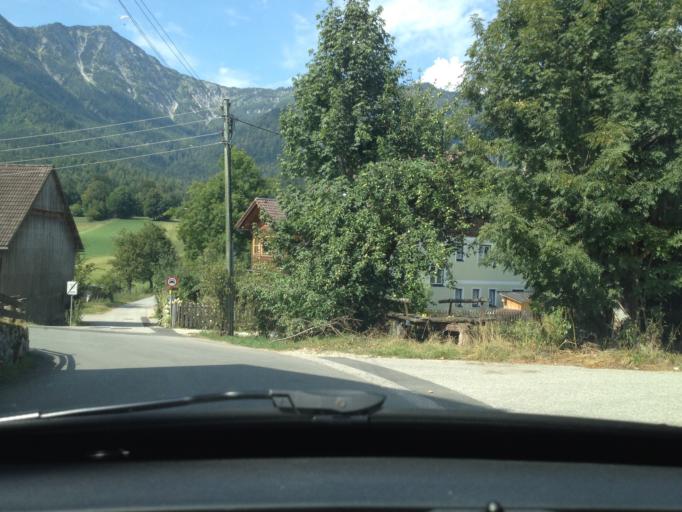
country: AT
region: Upper Austria
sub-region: Politischer Bezirk Gmunden
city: Bad Goisern
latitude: 47.6314
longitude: 13.6133
